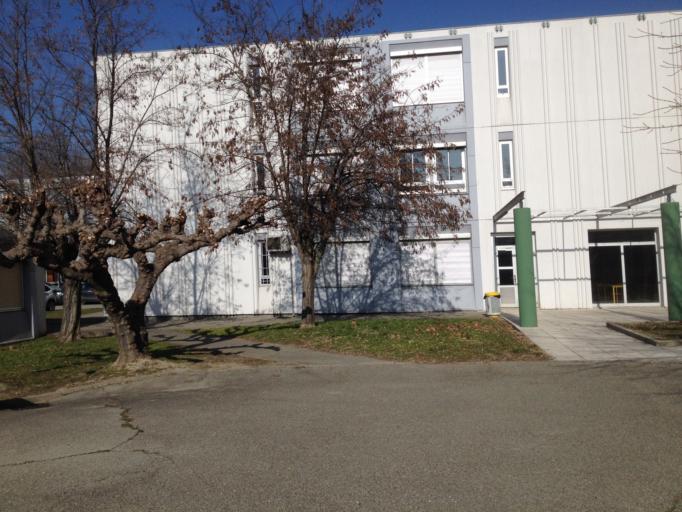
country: FR
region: Provence-Alpes-Cote d'Azur
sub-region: Departement du Vaucluse
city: Orange
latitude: 44.1311
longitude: 4.8271
